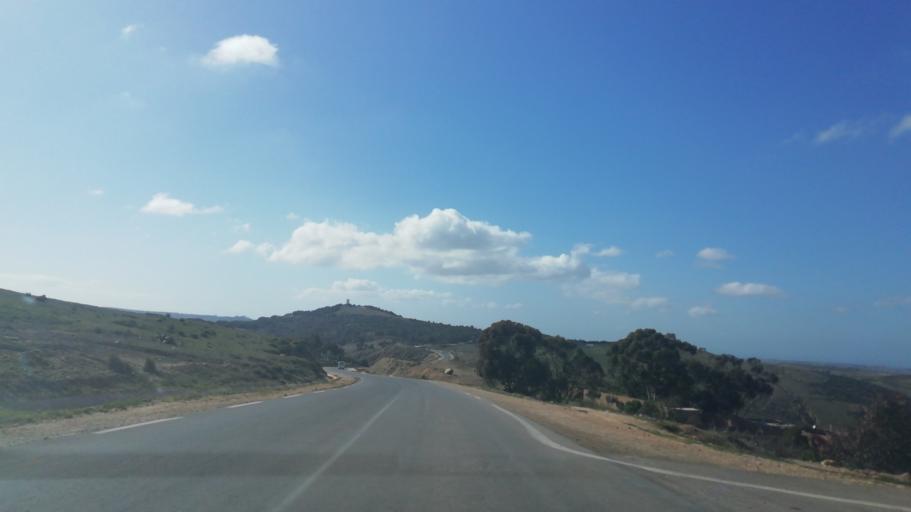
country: DZ
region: Relizane
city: Djidiouia
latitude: 36.0958
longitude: 0.5306
